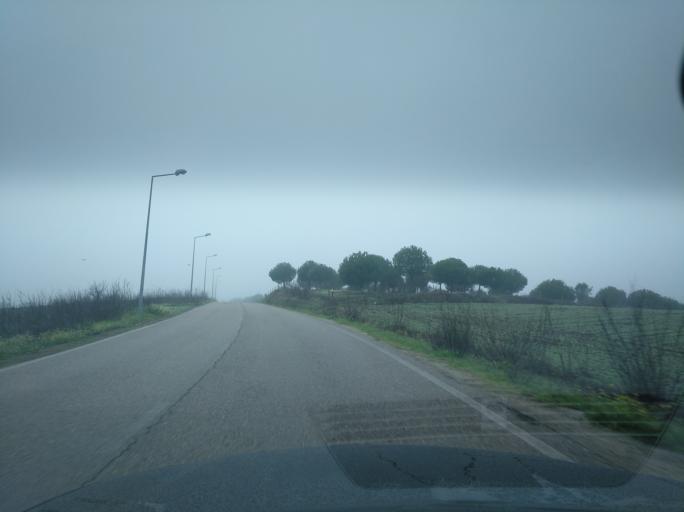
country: PT
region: Portalegre
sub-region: Campo Maior
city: Campo Maior
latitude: 39.0257
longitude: -7.0717
